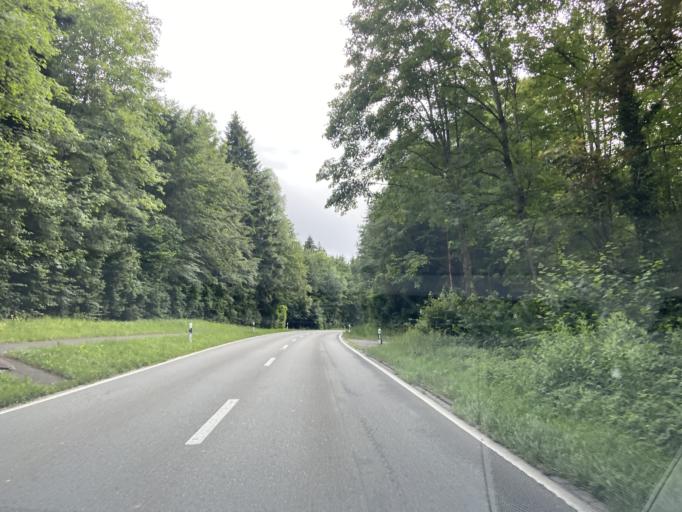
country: CH
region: Thurgau
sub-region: Muenchwilen District
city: Aadorf
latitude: 47.5014
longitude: 8.9158
